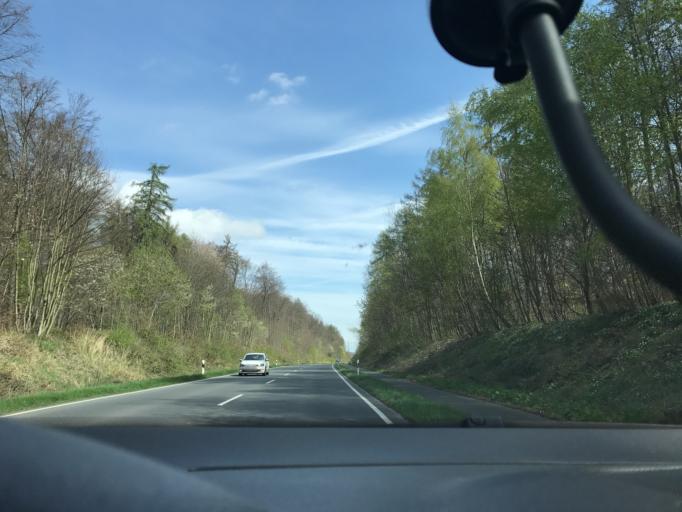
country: DE
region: Lower Saxony
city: Wolsdorf
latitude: 52.2020
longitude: 10.9713
